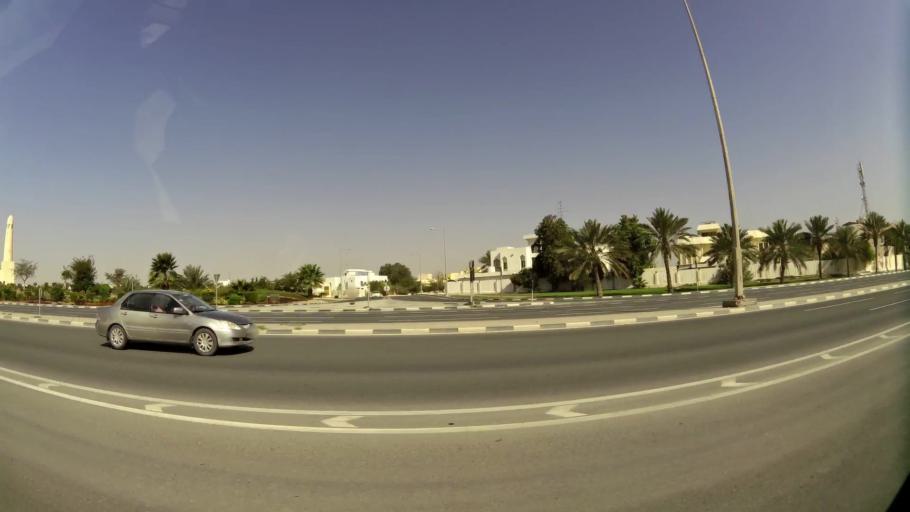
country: QA
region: Baladiyat ad Dawhah
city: Doha
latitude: 25.3178
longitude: 51.5101
